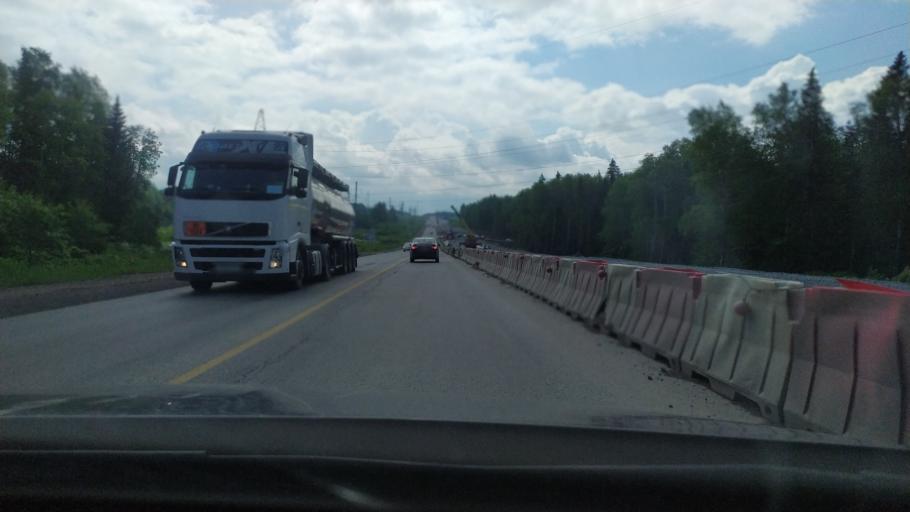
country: RU
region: Perm
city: Novyye Lyady
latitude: 58.0595
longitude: 56.4272
